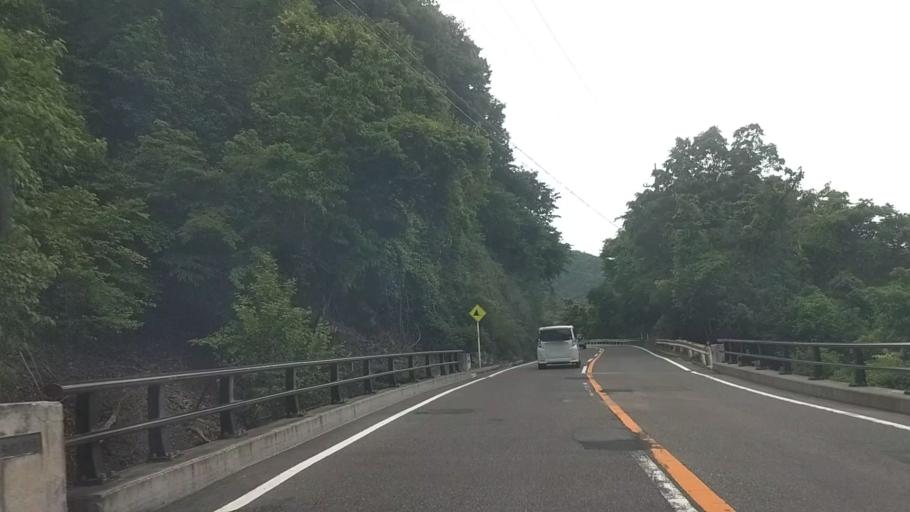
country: JP
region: Yamanashi
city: Fujikawaguchiko
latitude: 35.5211
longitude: 138.6216
